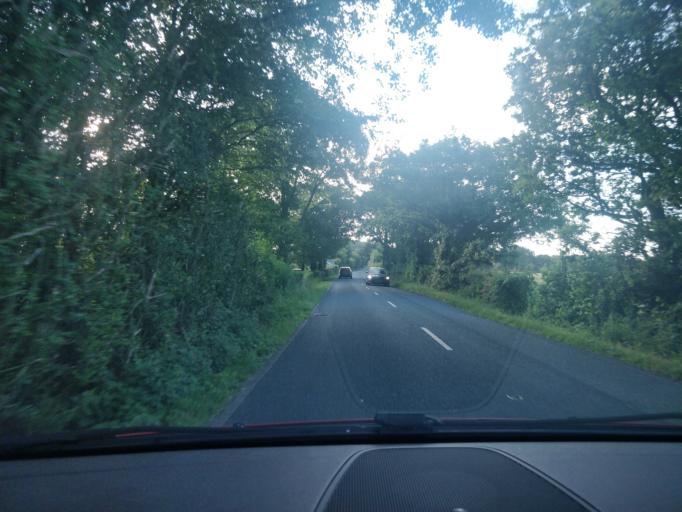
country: GB
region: England
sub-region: Lancashire
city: Skelmersdale
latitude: 53.5585
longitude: -2.7485
